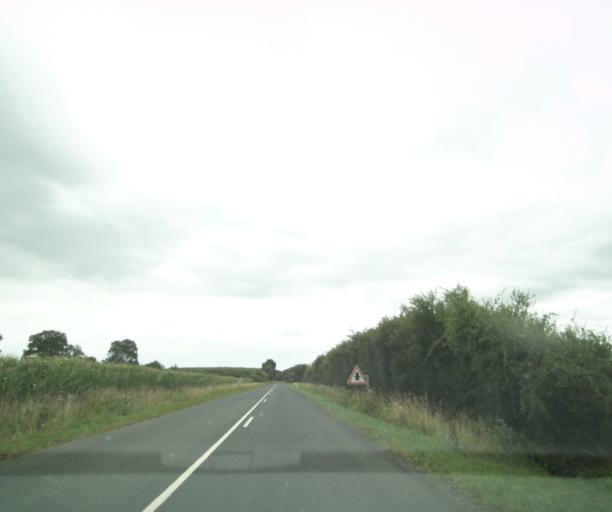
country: FR
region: Pays de la Loire
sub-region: Departement de la Sarthe
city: Precigne
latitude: 47.7505
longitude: -0.2978
